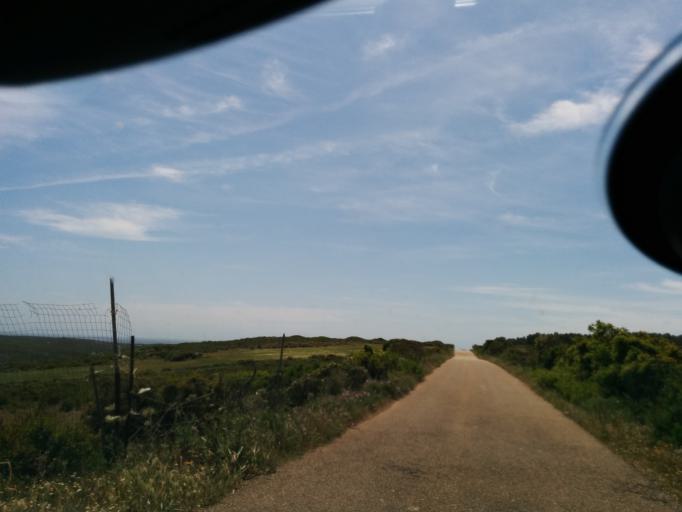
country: IT
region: Sardinia
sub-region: Provincia di Carbonia-Iglesias
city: Calasetta
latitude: 39.0401
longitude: 8.3800
